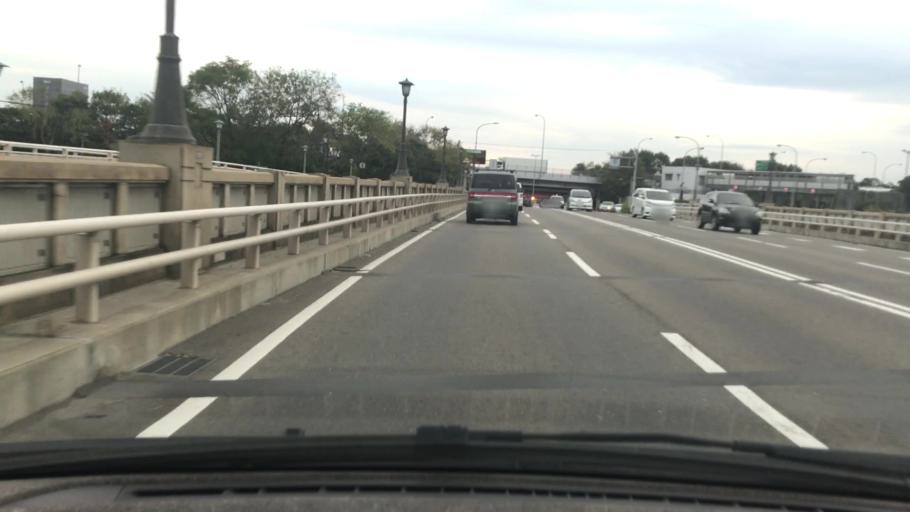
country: JP
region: Kyoto
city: Muko
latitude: 34.9557
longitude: 135.7456
